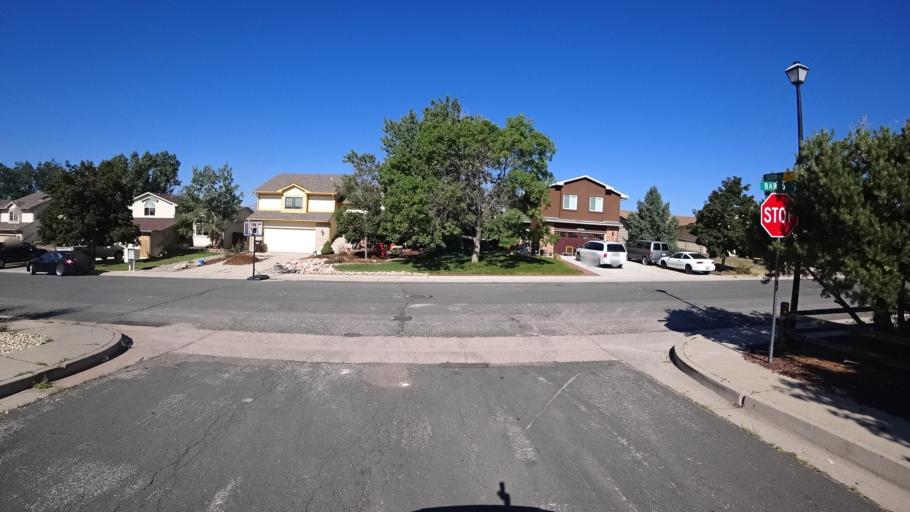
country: US
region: Colorado
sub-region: El Paso County
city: Black Forest
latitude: 38.9582
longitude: -104.7472
